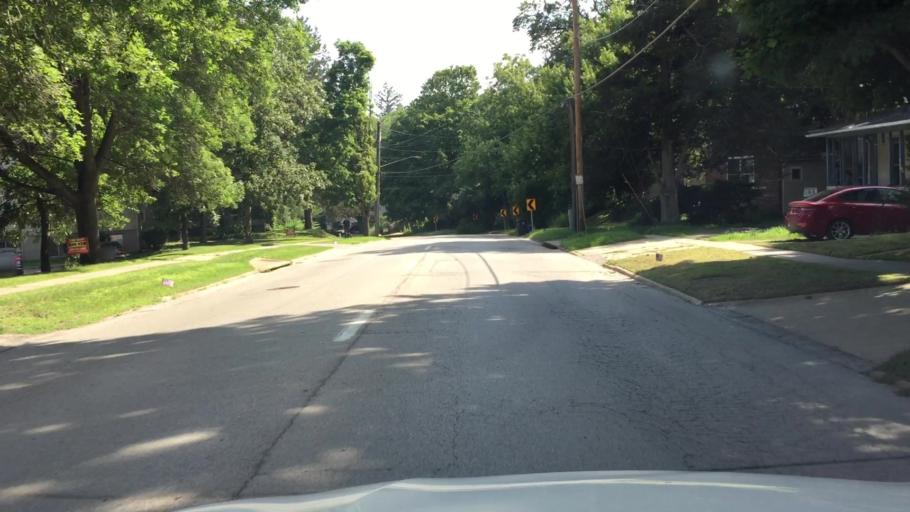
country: US
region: Iowa
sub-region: Johnson County
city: Iowa City
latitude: 41.6721
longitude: -91.5252
